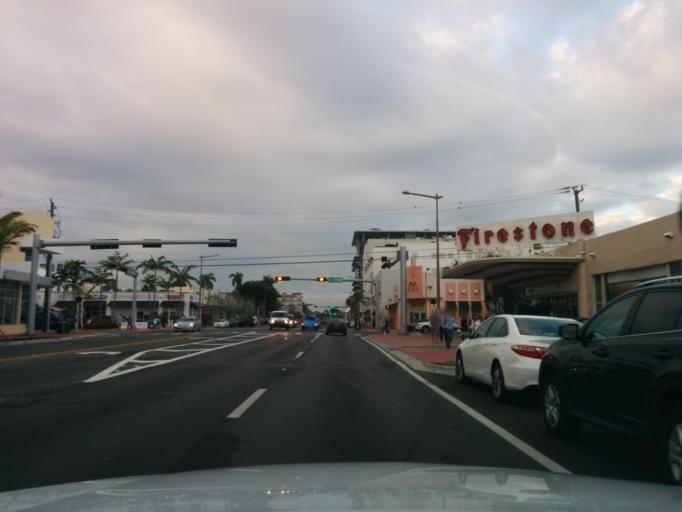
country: US
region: Florida
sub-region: Miami-Dade County
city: Miami Beach
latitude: 25.7883
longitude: -80.1411
